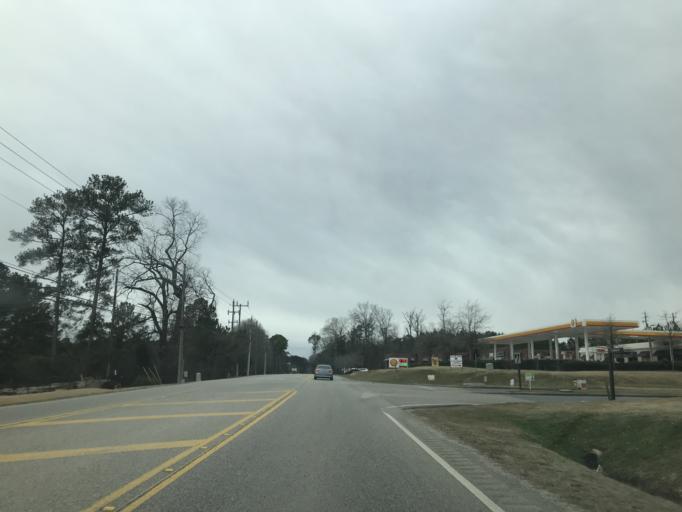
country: US
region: Alabama
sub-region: Shelby County
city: Brook Highland
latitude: 33.4361
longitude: -86.6624
